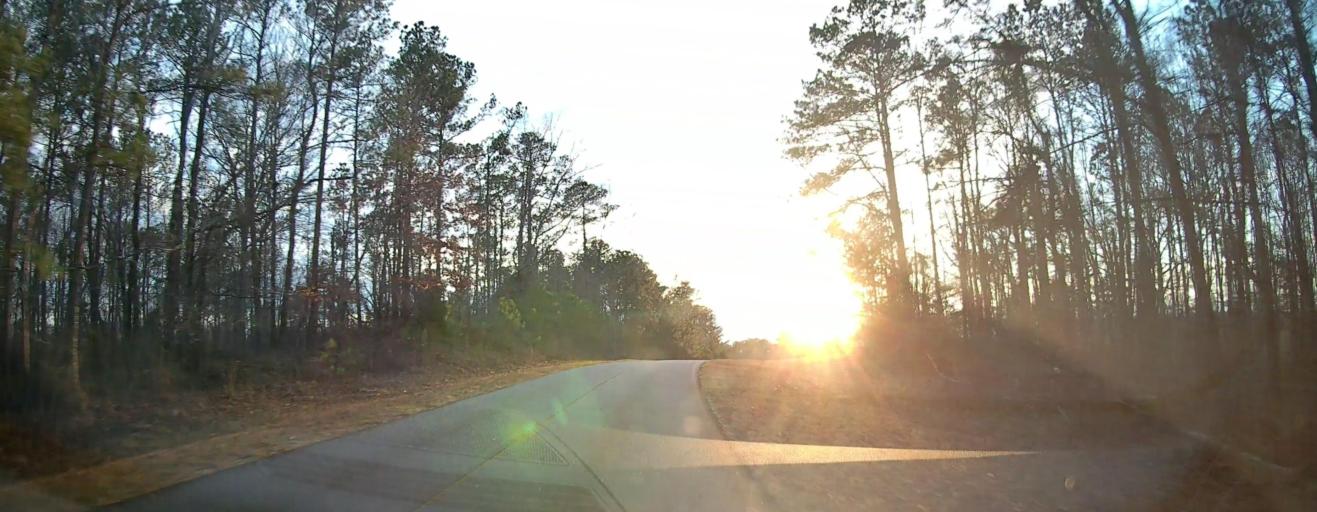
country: US
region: Georgia
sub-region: Harris County
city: Hamilton
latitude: 32.6056
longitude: -84.8723
